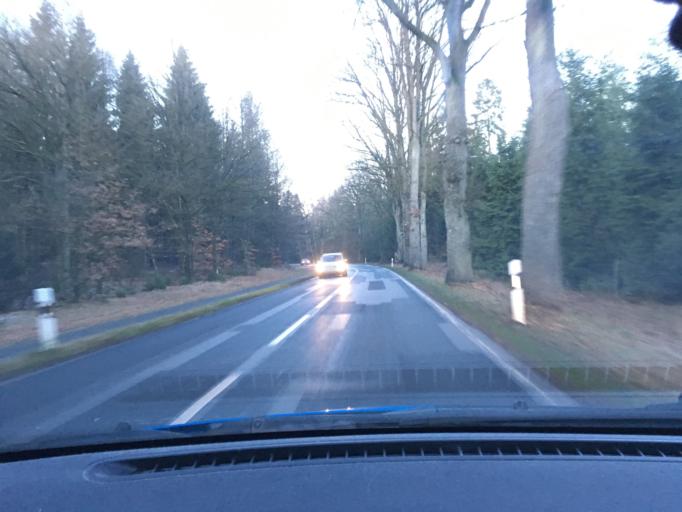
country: DE
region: Lower Saxony
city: Handeloh
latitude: 53.2719
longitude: 9.8788
